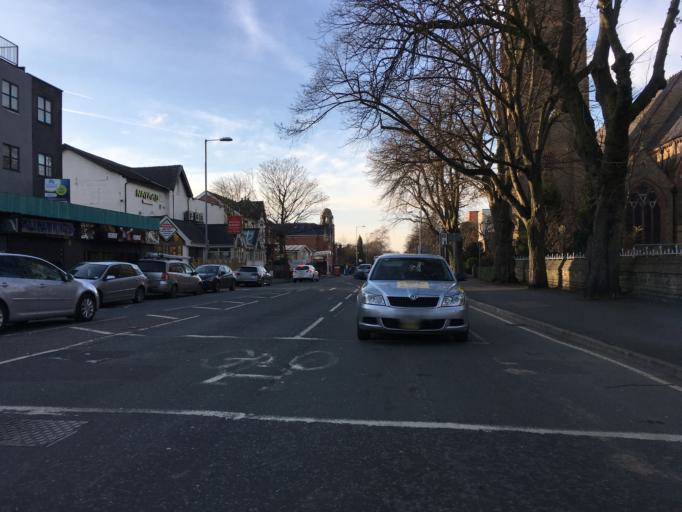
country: GB
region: England
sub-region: Manchester
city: Fallowfield
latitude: 53.4426
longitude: -2.2190
